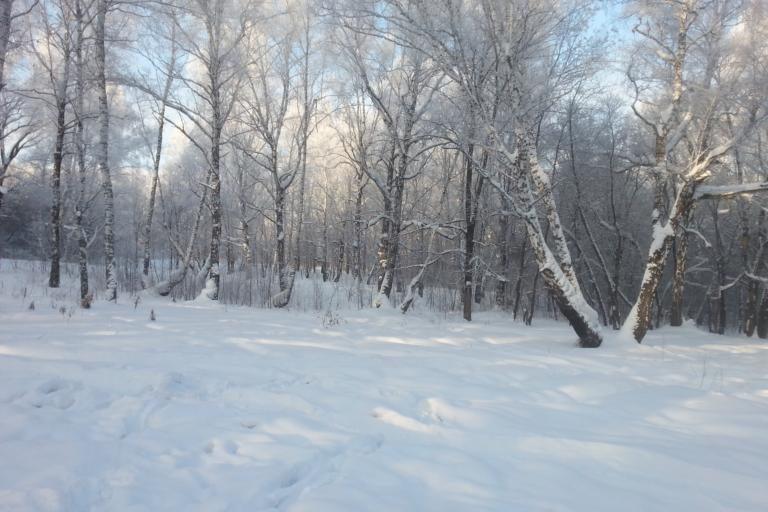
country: RU
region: Altai Krai
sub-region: Gorod Barnaulskiy
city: Barnaul
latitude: 53.3688
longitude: 83.7188
